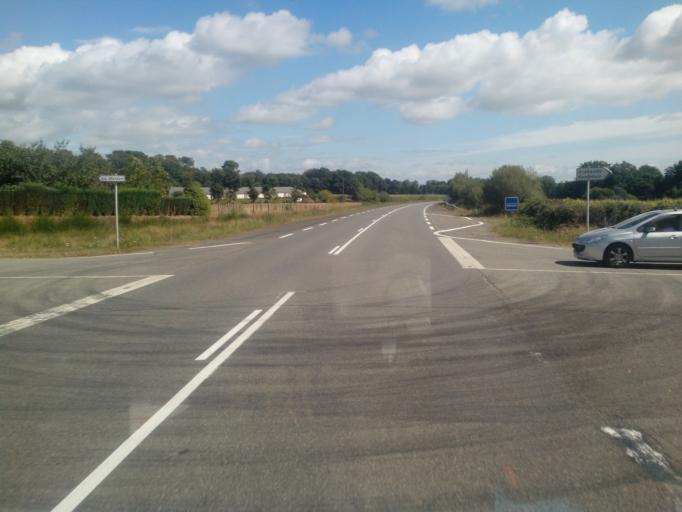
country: FR
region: Brittany
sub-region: Departement du Morbihan
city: Limerzel
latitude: 47.6127
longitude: -2.3928
